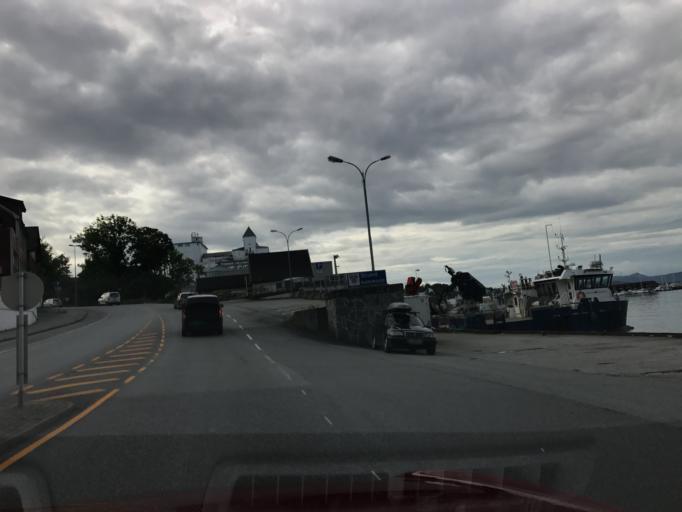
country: NO
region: Rogaland
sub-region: Strand
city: Tau
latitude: 59.0654
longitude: 5.9104
